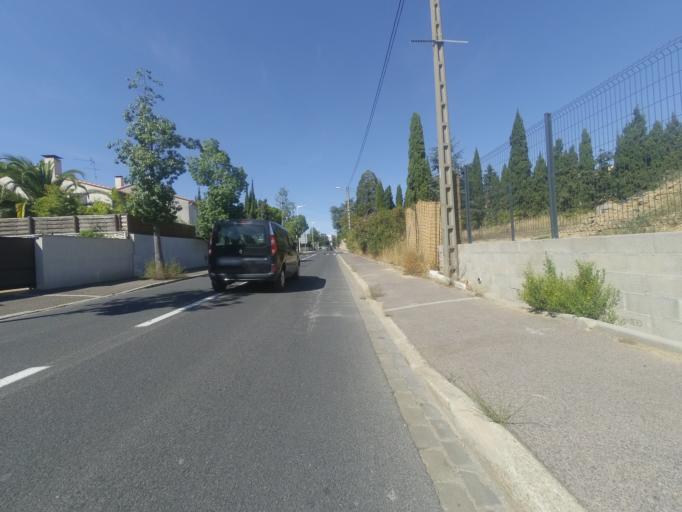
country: FR
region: Languedoc-Roussillon
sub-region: Departement des Pyrenees-Orientales
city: Perpignan
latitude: 42.6897
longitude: 2.9059
